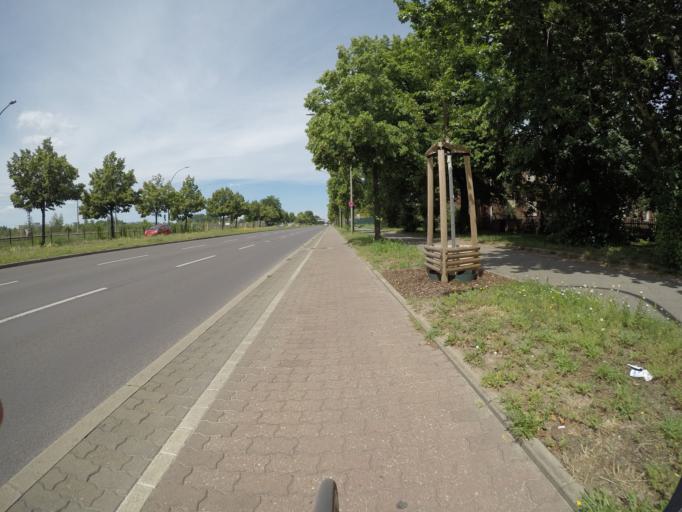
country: DE
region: Berlin
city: Niederschoneweide
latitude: 52.4439
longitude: 13.5290
